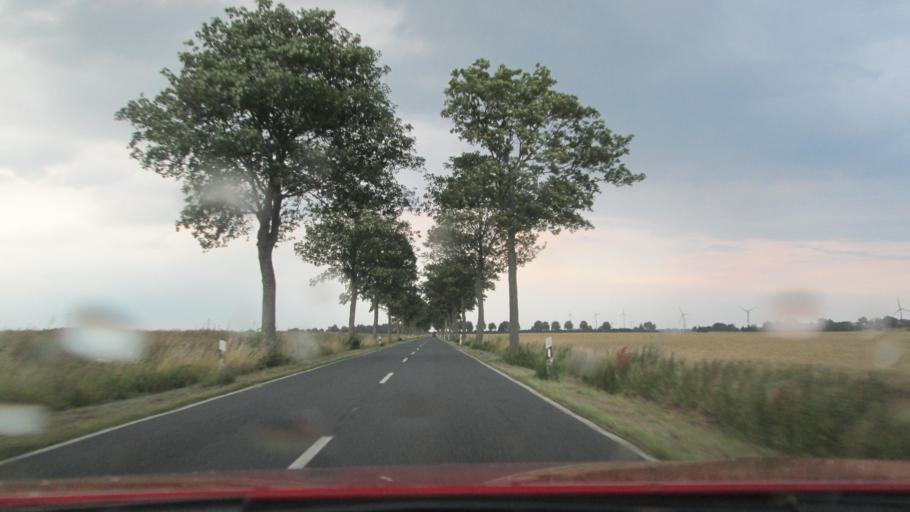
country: DE
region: Lower Saxony
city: Calberlah
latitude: 52.3775
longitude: 10.6404
